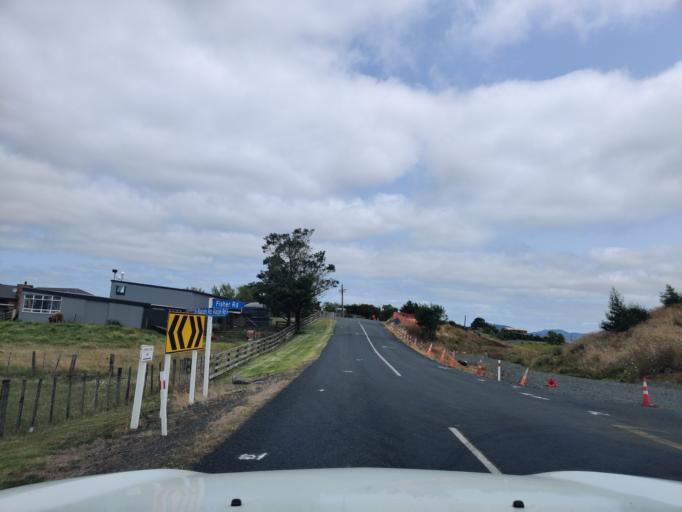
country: NZ
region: Waikato
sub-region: Waikato District
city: Te Kauwhata
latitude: -37.5188
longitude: 175.1771
